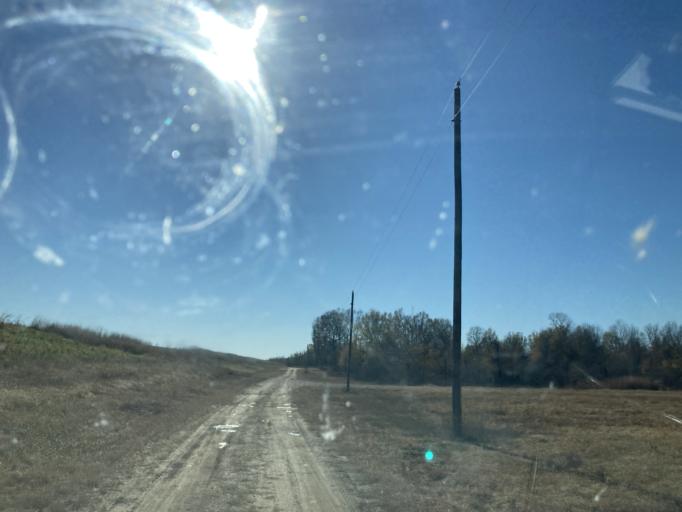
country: US
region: Mississippi
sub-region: Sharkey County
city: Rolling Fork
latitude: 32.7522
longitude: -90.6601
